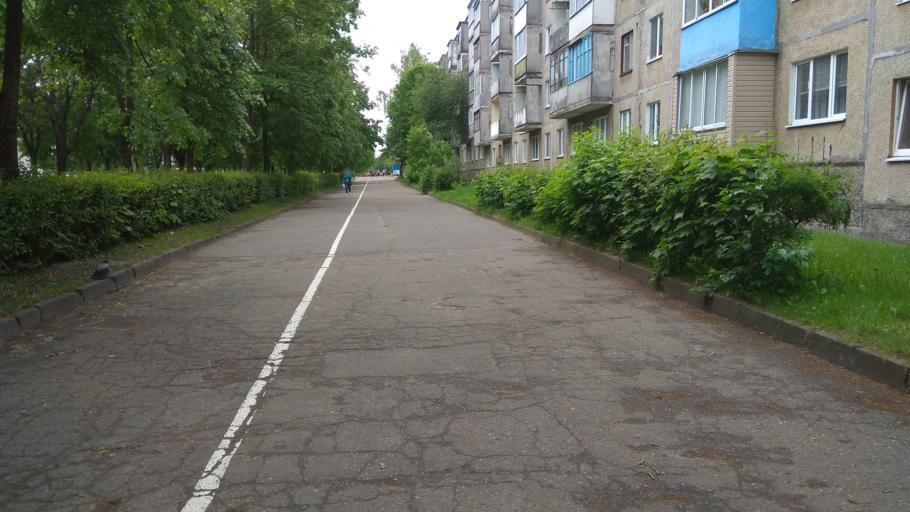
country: BY
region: Grodnenskaya
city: Hrodna
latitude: 53.7057
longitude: 23.8052
